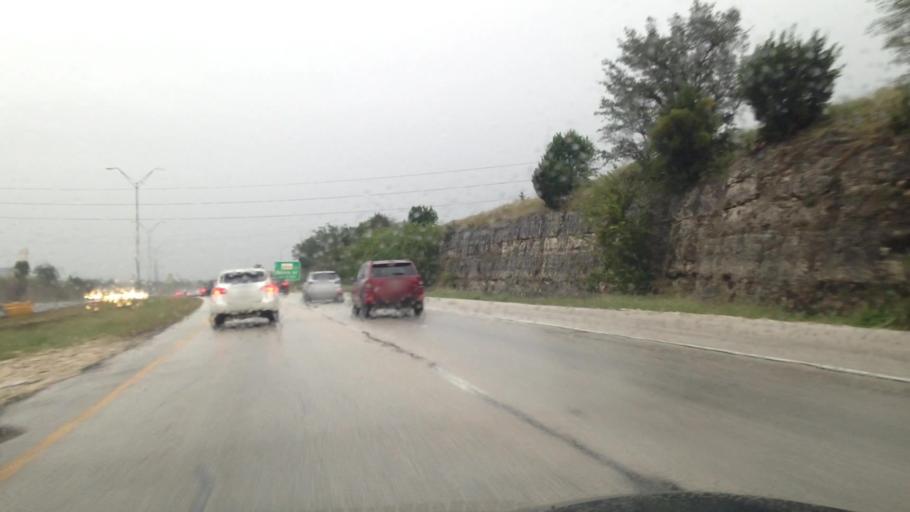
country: US
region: Texas
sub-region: Bexar County
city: Shavano Park
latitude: 29.6045
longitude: -98.5333
